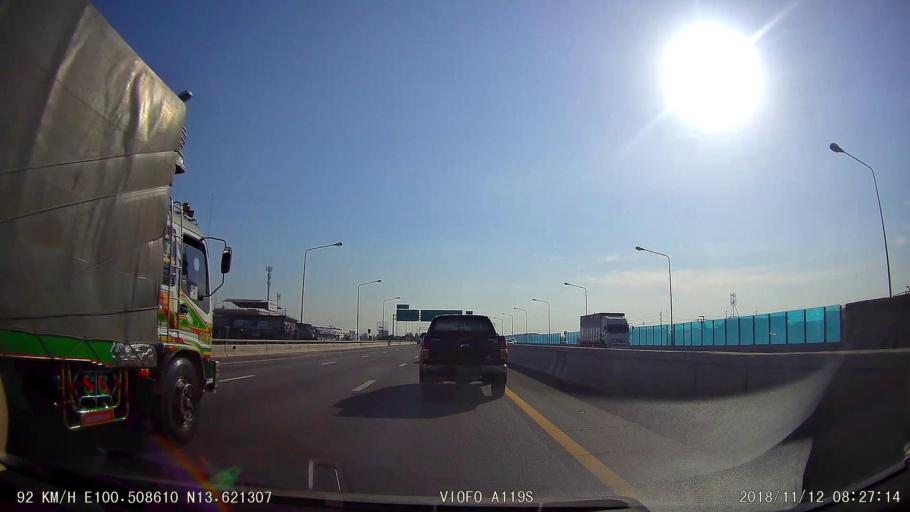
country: TH
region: Bangkok
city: Thung Khru
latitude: 13.6214
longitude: 100.5098
